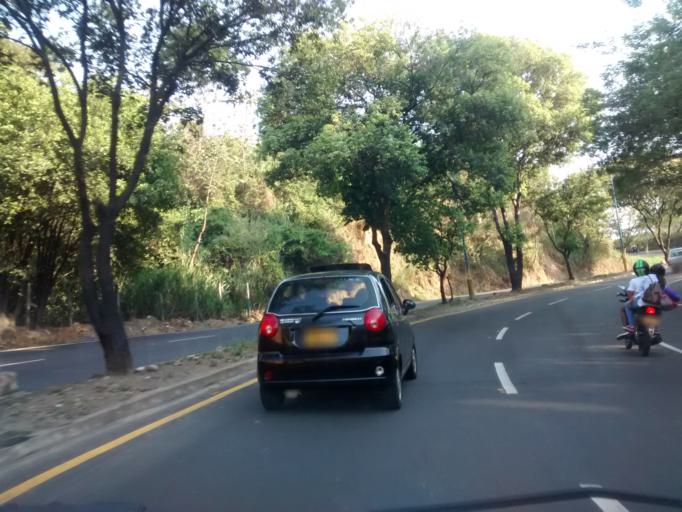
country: CO
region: Santander
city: Bucaramanga
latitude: 7.0913
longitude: -73.1315
